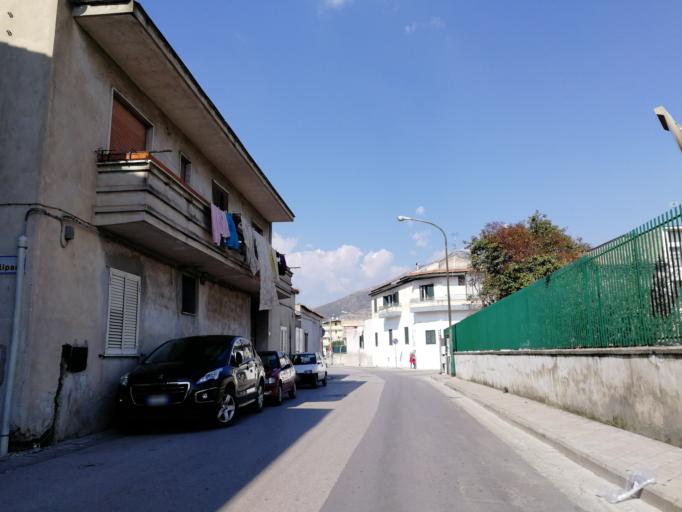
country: IT
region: Campania
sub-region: Provincia di Caserta
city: San Prisco
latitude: 41.0875
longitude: 14.2737
